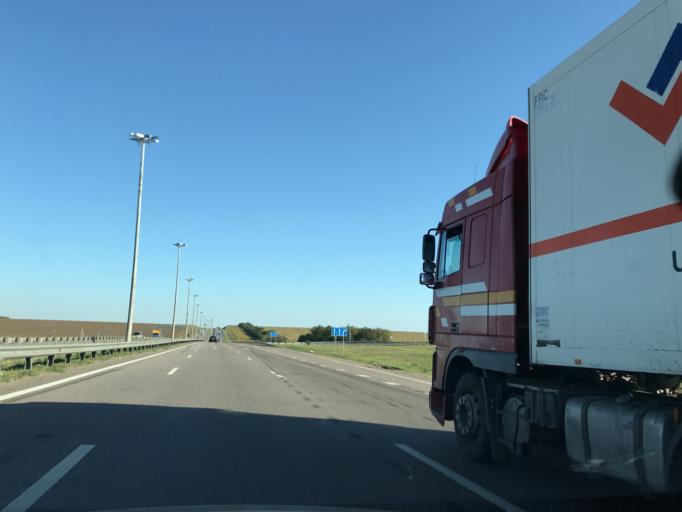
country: RU
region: Rostov
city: Glubokiy
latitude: 48.4508
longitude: 40.3408
